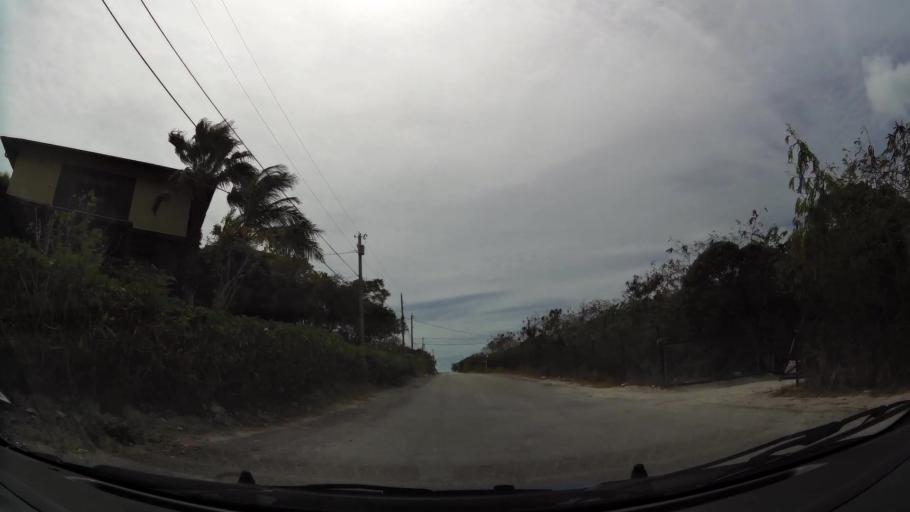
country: BS
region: Mayaguana
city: Abraham's Bay
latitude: 21.7838
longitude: -72.2351
